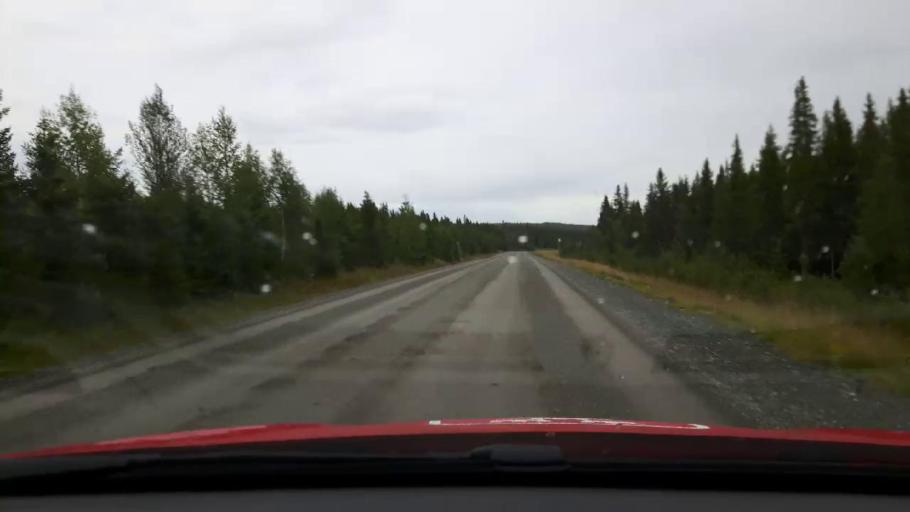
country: SE
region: Jaemtland
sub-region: Are Kommun
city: Are
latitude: 63.4682
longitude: 12.6086
